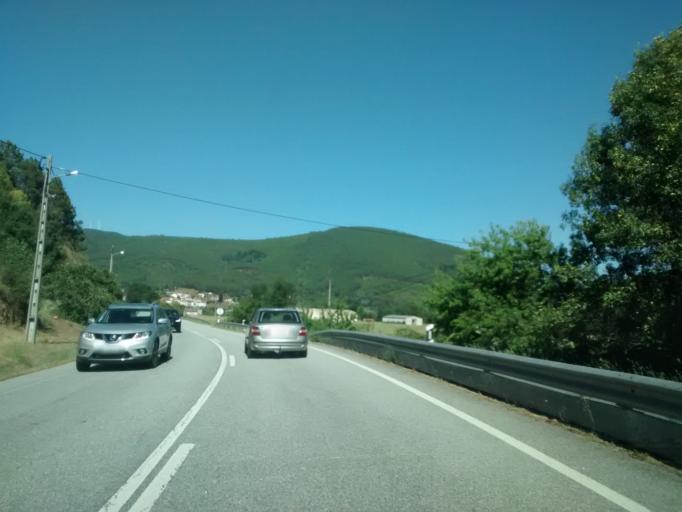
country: PT
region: Castelo Branco
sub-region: Belmonte
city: Belmonte
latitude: 40.4010
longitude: -7.4144
